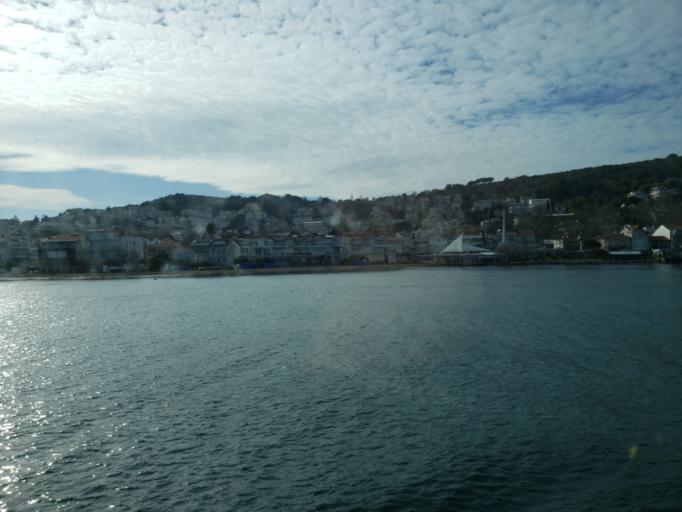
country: TR
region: Istanbul
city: Kinali
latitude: 40.9089
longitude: 29.0578
